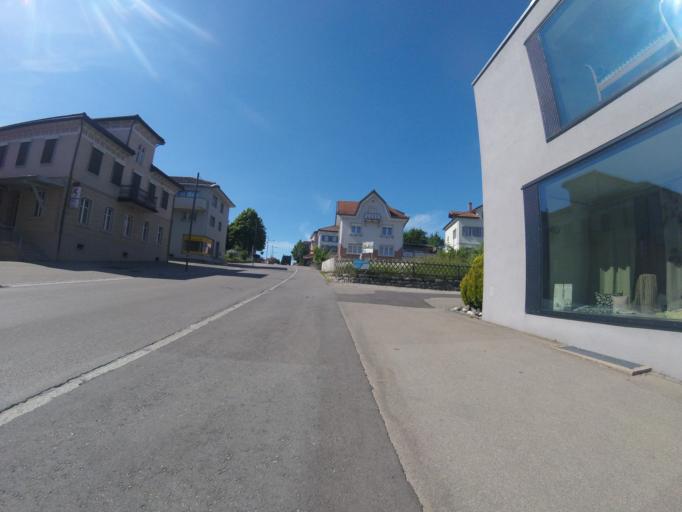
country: CH
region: Saint Gallen
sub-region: Wahlkreis Wil
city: Jonschwil
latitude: 47.4139
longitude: 9.0680
